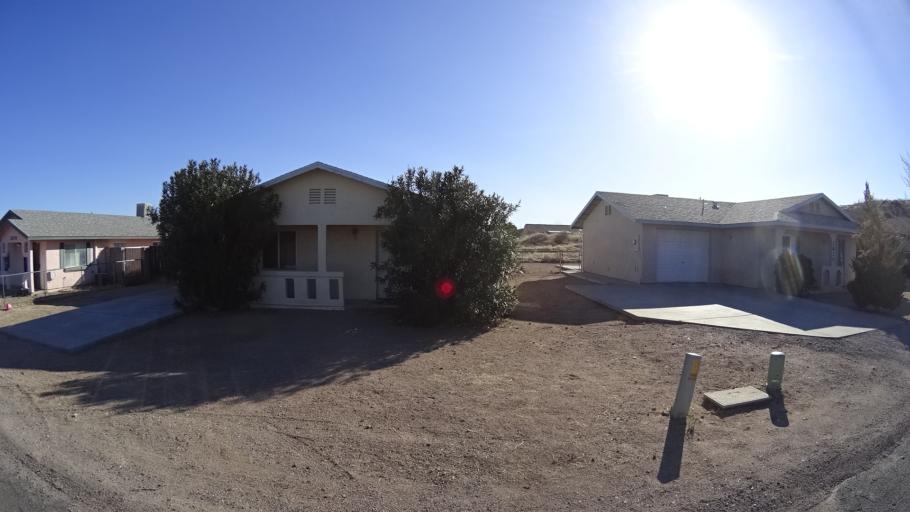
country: US
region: Arizona
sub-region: Mohave County
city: Kingman
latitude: 35.2114
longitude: -114.0093
